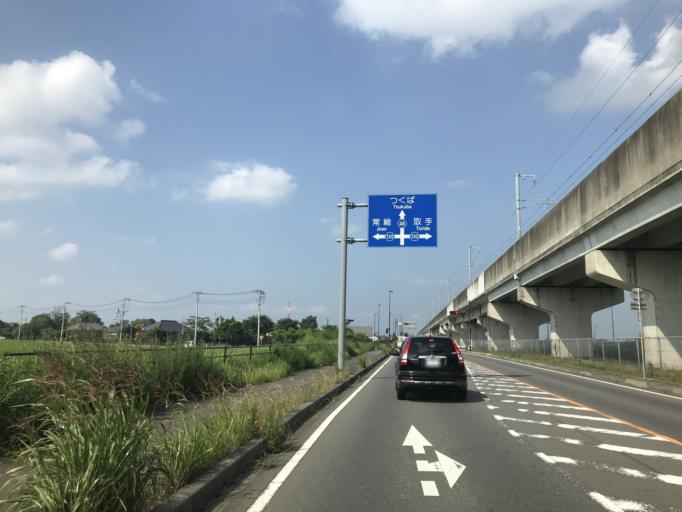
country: JP
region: Ibaraki
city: Moriya
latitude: 35.9765
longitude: 140.0209
